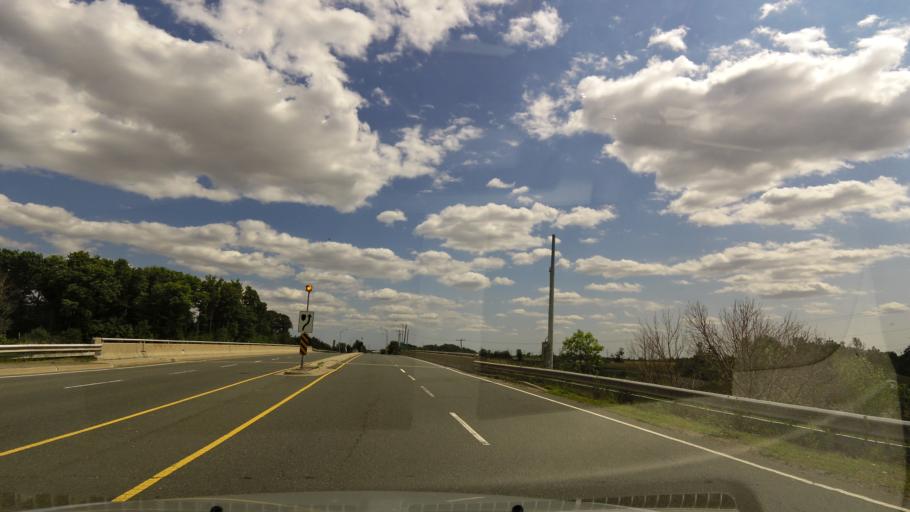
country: CA
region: Ontario
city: Ancaster
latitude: 43.2019
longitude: -80.0451
